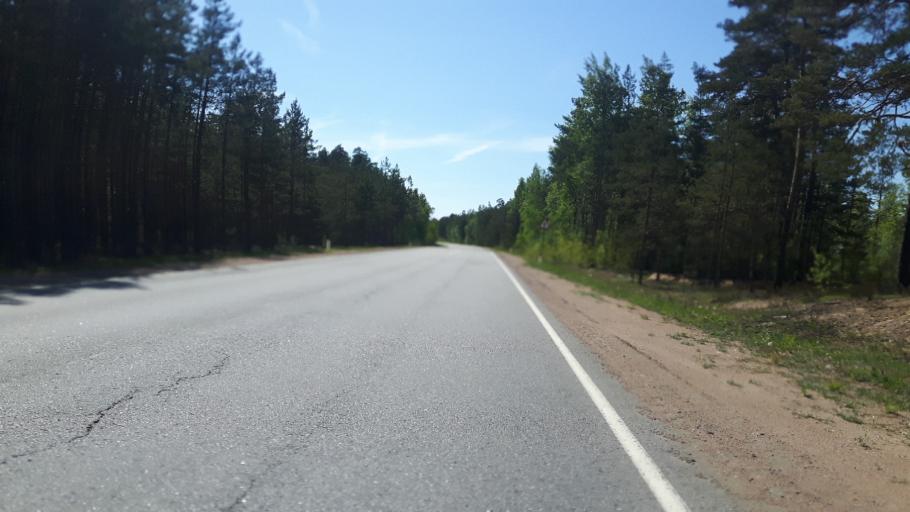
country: RU
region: Leningrad
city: Sista-Palkino
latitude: 59.7692
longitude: 28.7687
